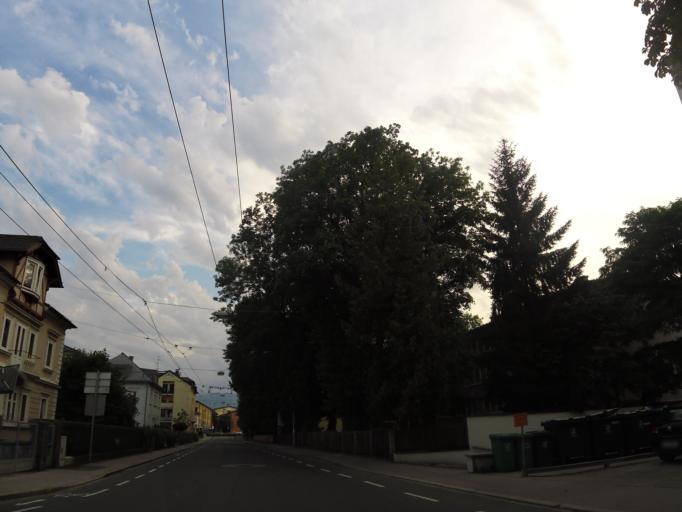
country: AT
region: Salzburg
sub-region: Salzburg Stadt
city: Salzburg
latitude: 47.7979
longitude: 13.0299
